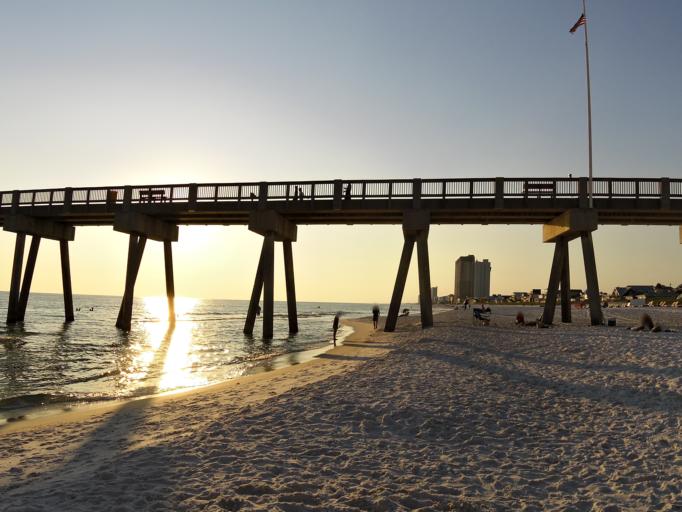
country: US
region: Florida
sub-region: Bay County
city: Laguna Beach
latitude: 30.2147
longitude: -85.8775
